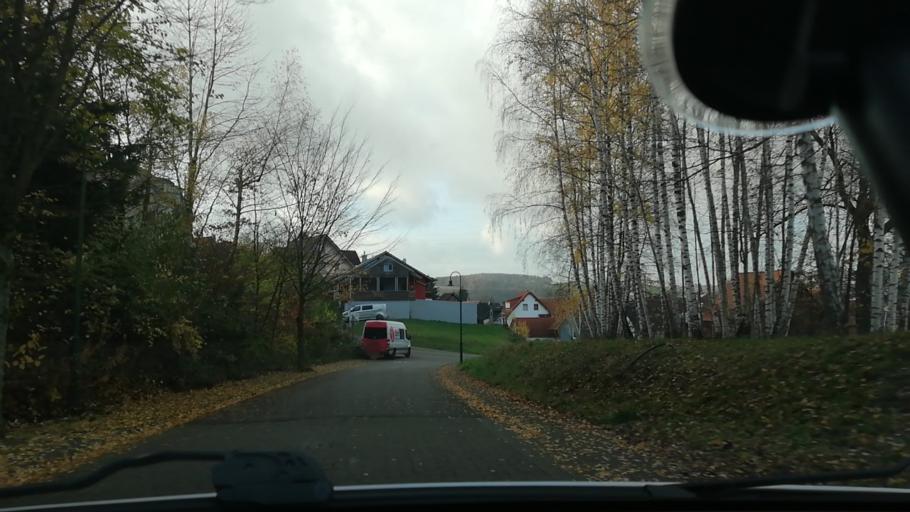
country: DE
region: Bavaria
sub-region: Regierungsbezirk Unterfranken
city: Sommerkahl
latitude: 50.0687
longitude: 9.2537
